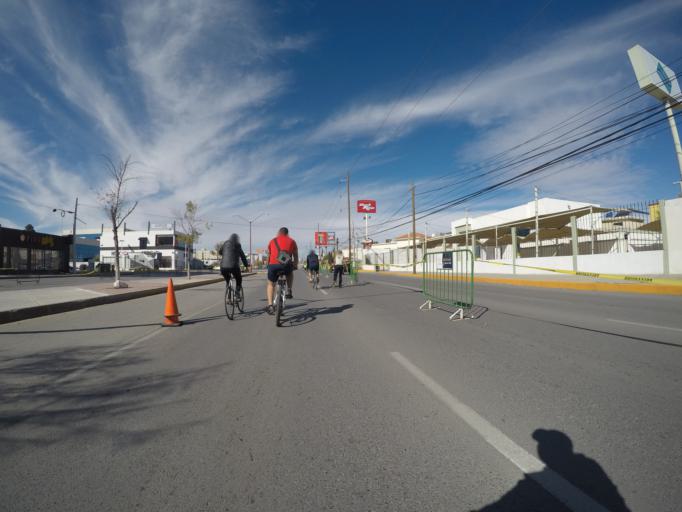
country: MX
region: Chihuahua
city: Ciudad Juarez
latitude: 31.7288
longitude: -106.4076
